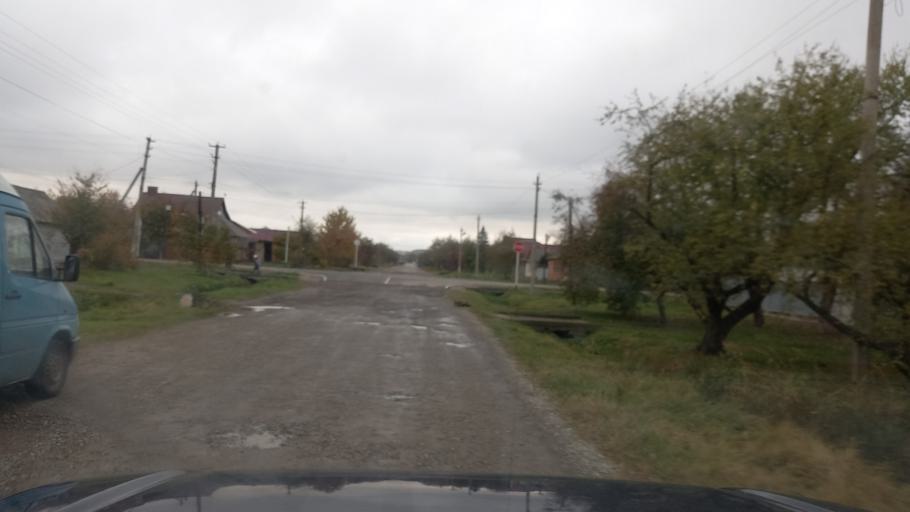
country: RU
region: Adygeya
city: Maykop
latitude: 44.6194
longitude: 40.1262
